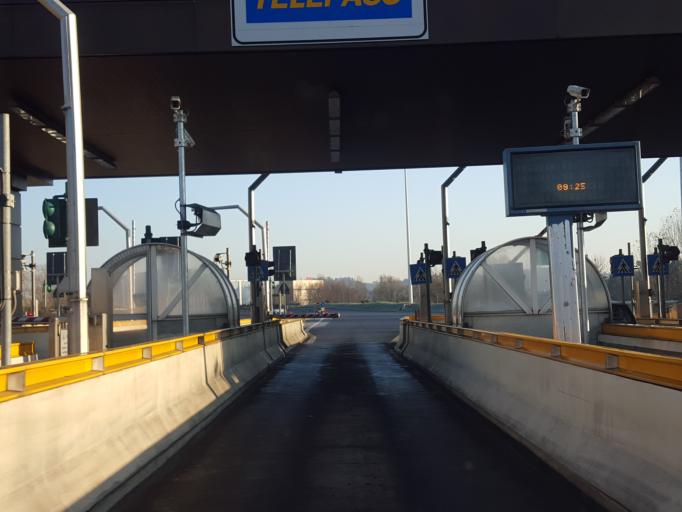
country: IT
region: Veneto
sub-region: Provincia di Vicenza
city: Creazzo
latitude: 45.5155
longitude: 11.5057
